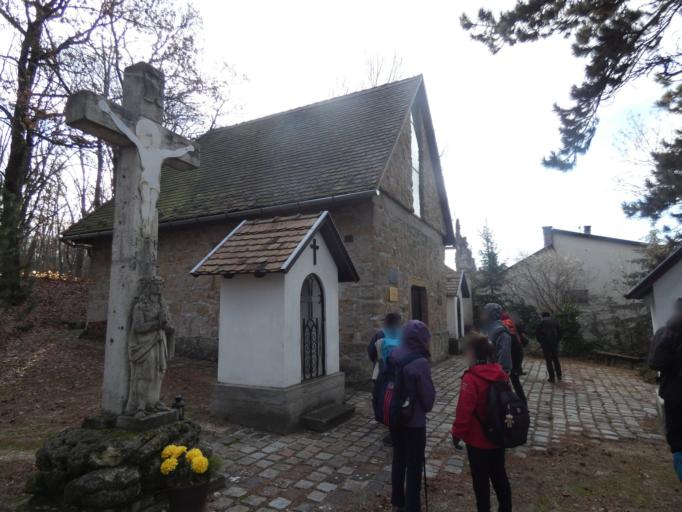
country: HU
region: Pest
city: Budakeszi
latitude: 47.5088
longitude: 18.9348
